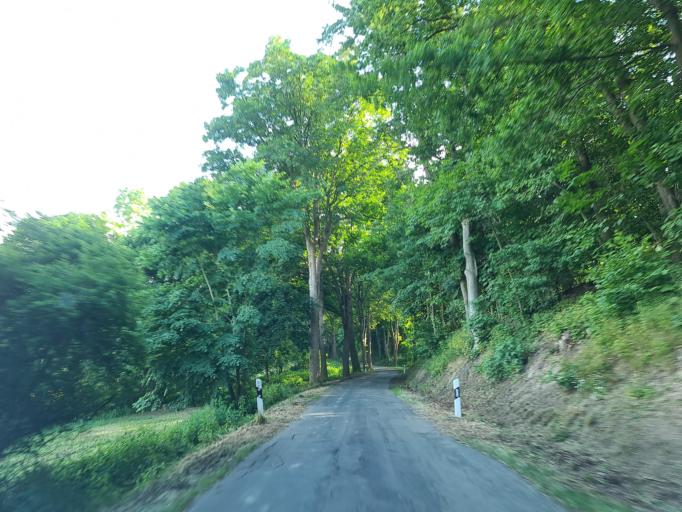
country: DE
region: Saxony
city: Bosenbrunn
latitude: 50.4031
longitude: 12.0959
